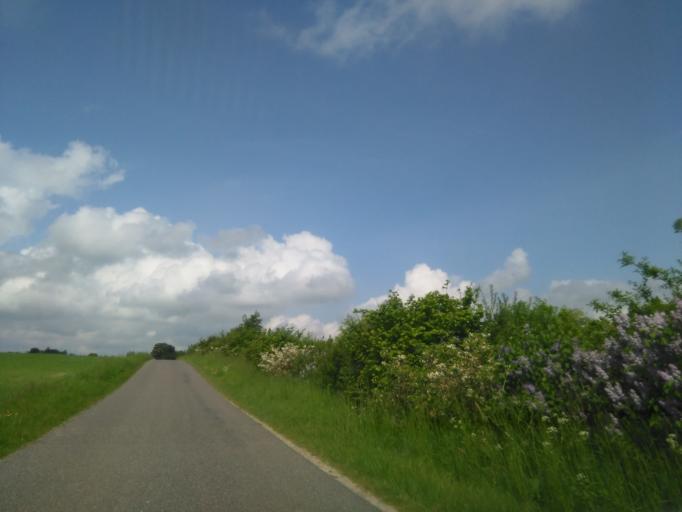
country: DK
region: Central Jutland
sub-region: Skanderborg Kommune
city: Skovby
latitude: 56.2054
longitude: 9.9502
